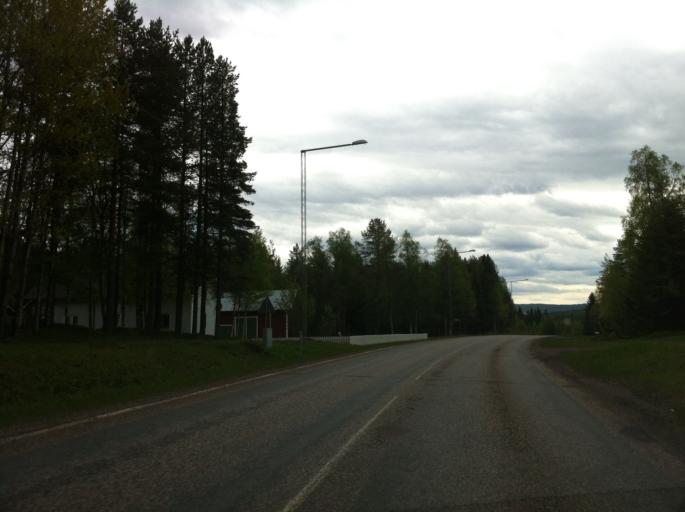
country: SE
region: Dalarna
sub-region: Malung-Saelens kommun
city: Malung
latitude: 61.0646
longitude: 13.3322
